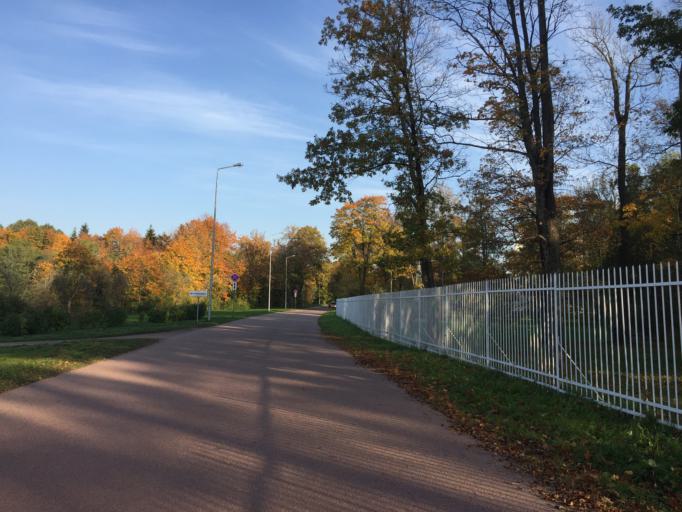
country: RU
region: St.-Petersburg
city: Pushkin
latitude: 59.7249
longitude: 30.3862
